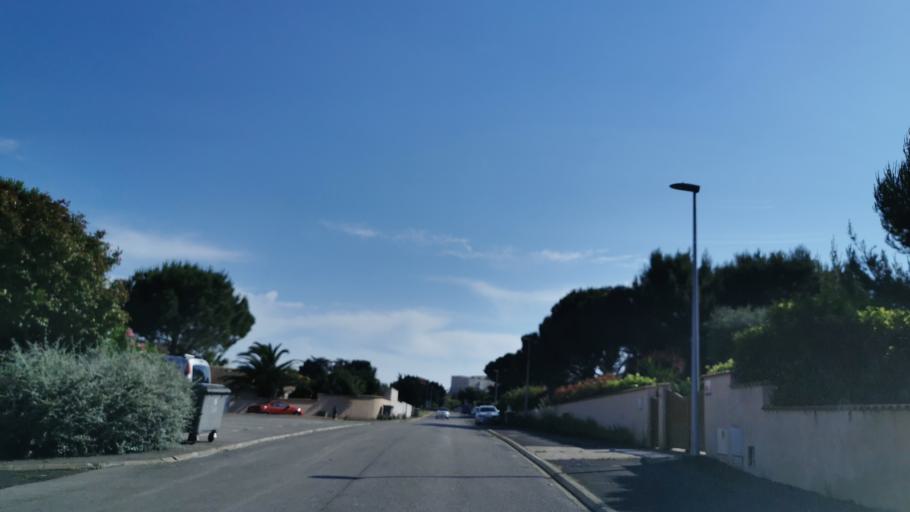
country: FR
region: Languedoc-Roussillon
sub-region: Departement de l'Aude
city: Narbonne
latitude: 43.1427
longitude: 2.9679
